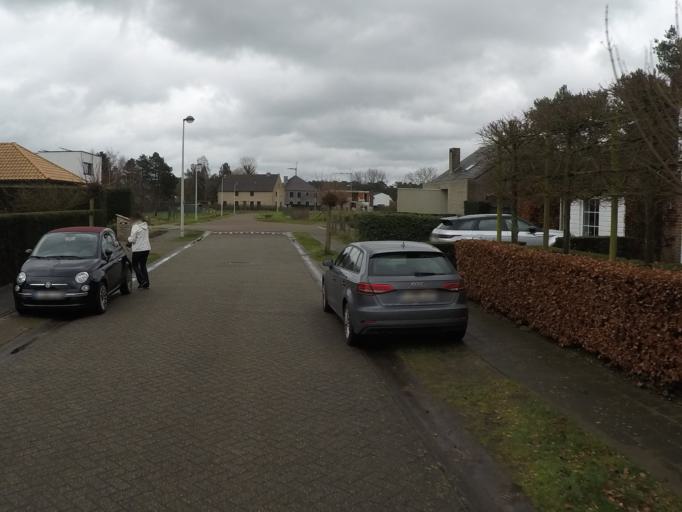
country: BE
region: Flanders
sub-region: Provincie Antwerpen
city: Schilde
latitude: 51.2146
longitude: 4.6009
